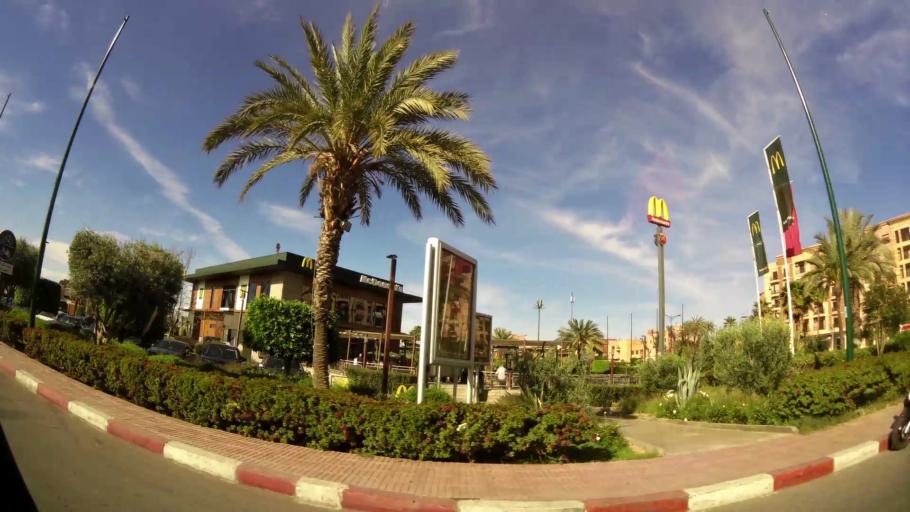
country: MA
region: Marrakech-Tensift-Al Haouz
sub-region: Marrakech
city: Marrakesh
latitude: 31.6547
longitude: -8.0196
